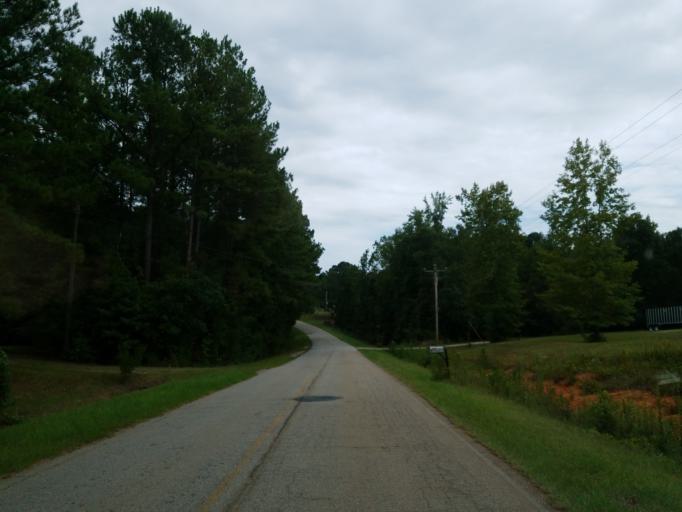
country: US
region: Georgia
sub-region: Monroe County
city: Forsyth
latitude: 32.9703
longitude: -83.9784
